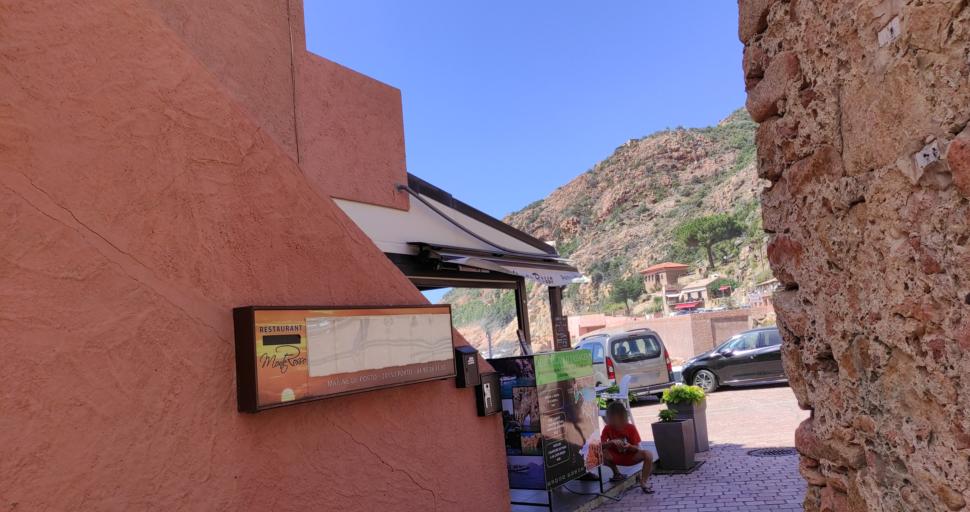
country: FR
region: Corsica
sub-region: Departement de la Corse-du-Sud
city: Cargese
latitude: 42.2678
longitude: 8.6934
